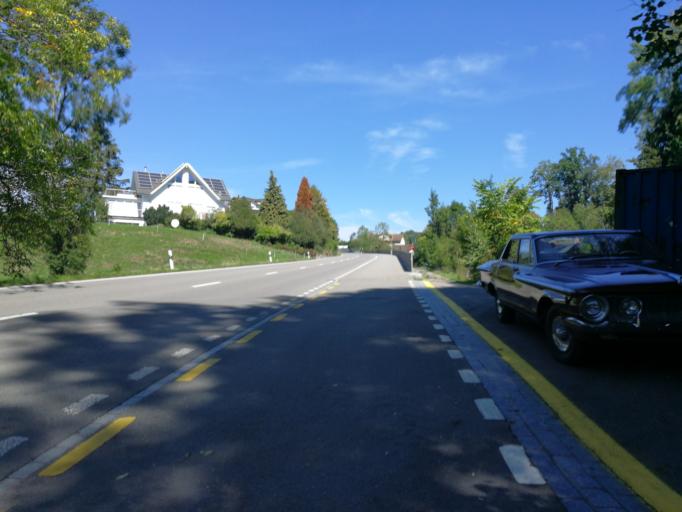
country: CH
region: Zurich
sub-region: Bezirk Hinwil
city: Durnten
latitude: 47.2835
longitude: 8.8428
